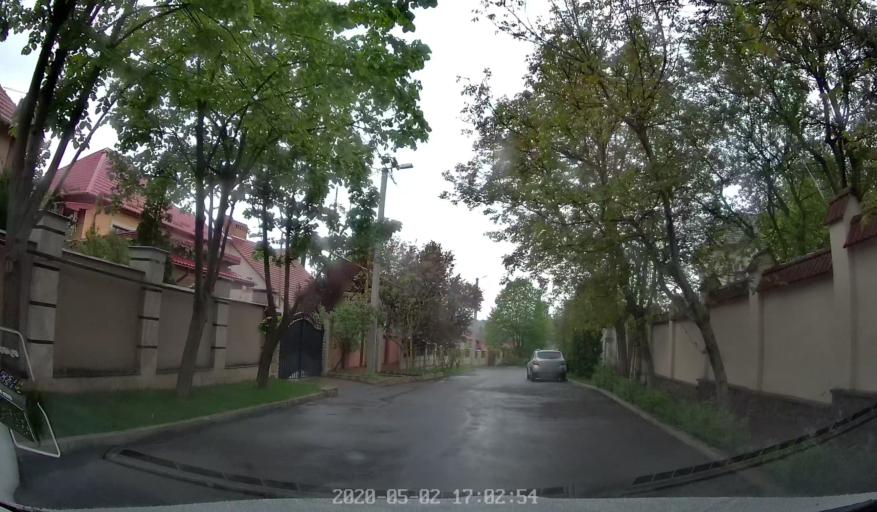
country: MD
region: Chisinau
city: Chisinau
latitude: 46.9708
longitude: 28.8329
